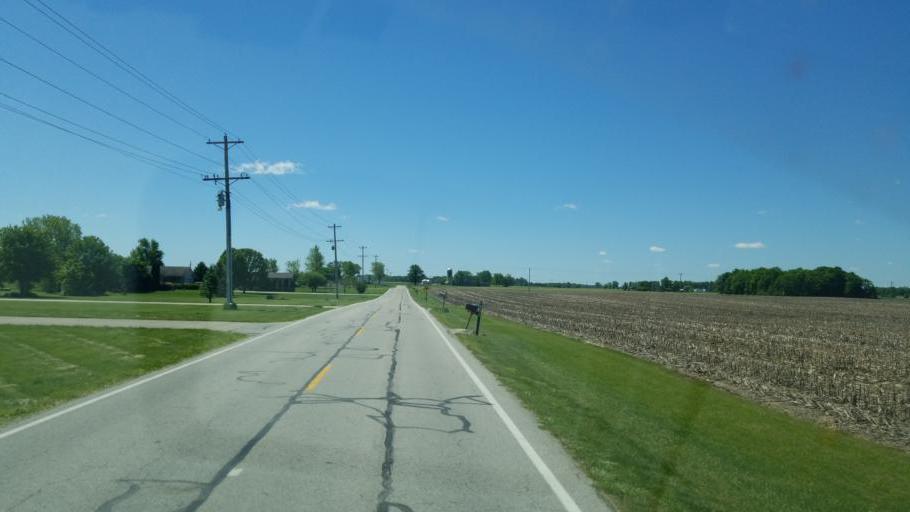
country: US
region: Ohio
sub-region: Shelby County
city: Anna
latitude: 40.3753
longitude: -84.2403
